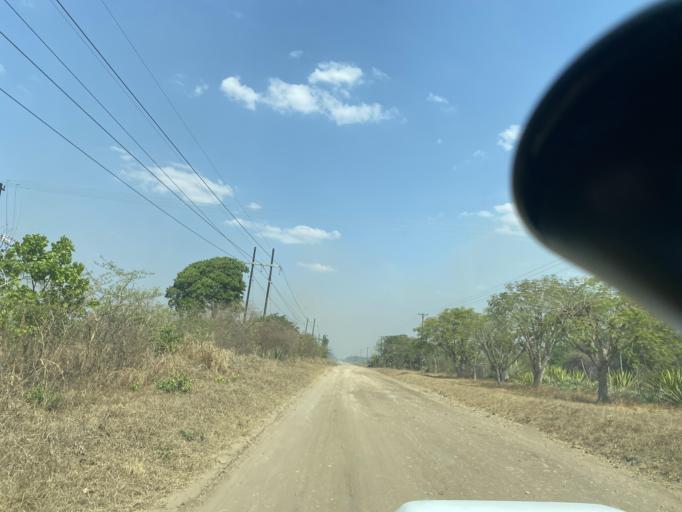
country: ZM
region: Lusaka
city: Lusaka
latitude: -15.3032
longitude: 28.0335
